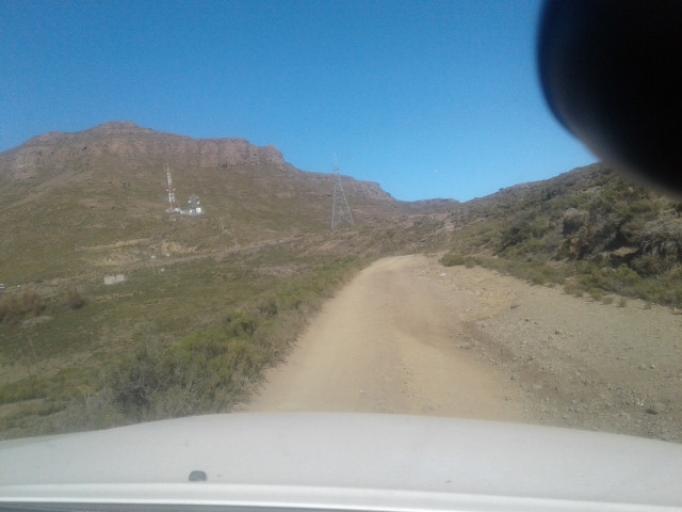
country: LS
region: Maseru
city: Nako
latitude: -29.4287
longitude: 27.9689
